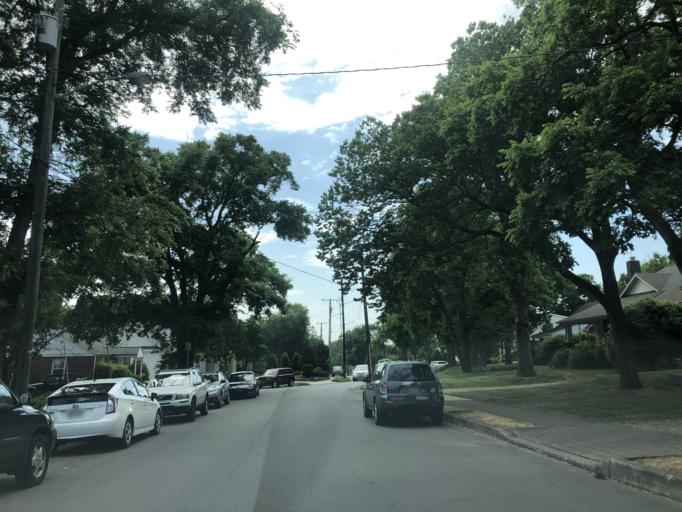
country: US
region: Tennessee
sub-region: Davidson County
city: Nashville
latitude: 36.1267
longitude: -86.8015
